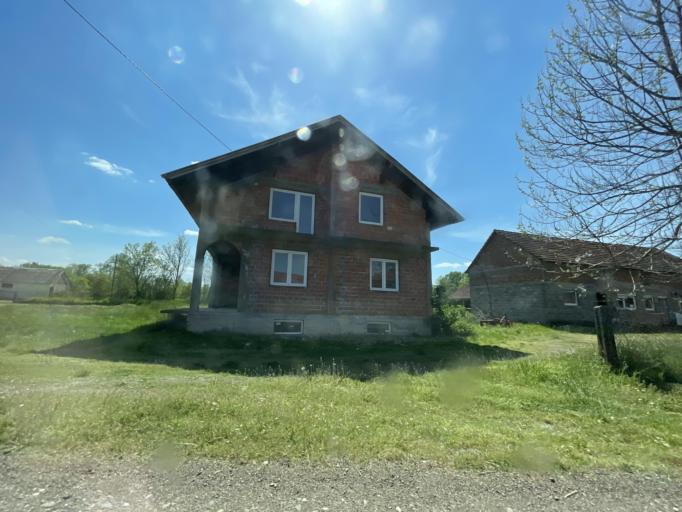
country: BA
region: Federation of Bosnia and Herzegovina
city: Donja Dubica
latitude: 45.0303
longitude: 18.4155
